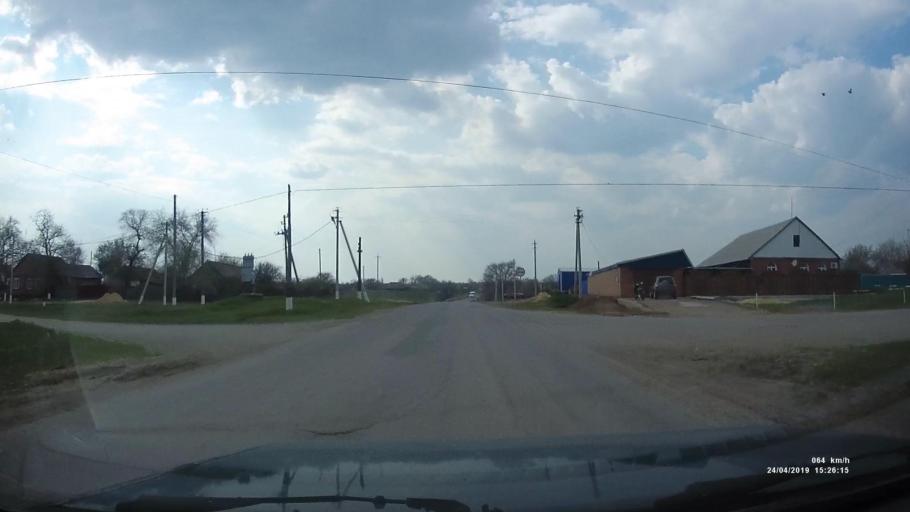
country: RU
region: Rostov
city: Remontnoye
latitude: 46.5578
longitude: 43.0347
